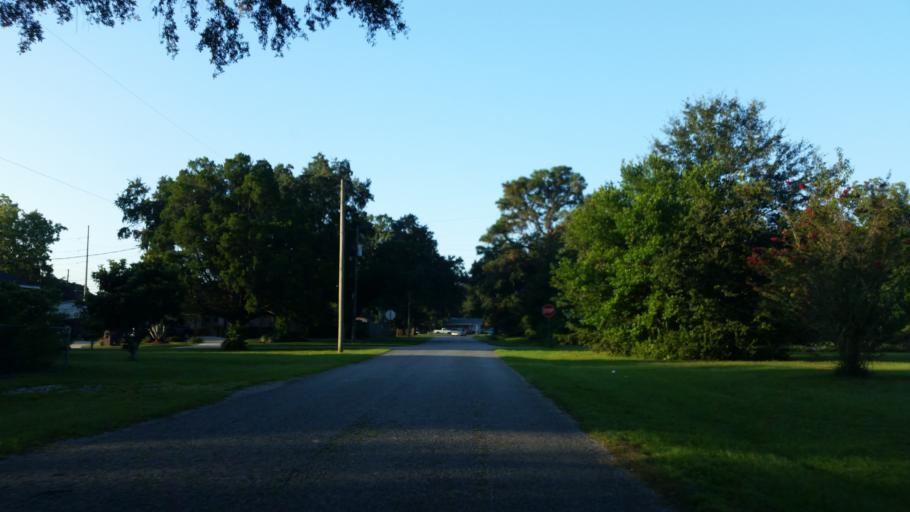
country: US
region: Florida
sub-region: Escambia County
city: Ferry Pass
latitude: 30.5308
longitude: -87.2065
